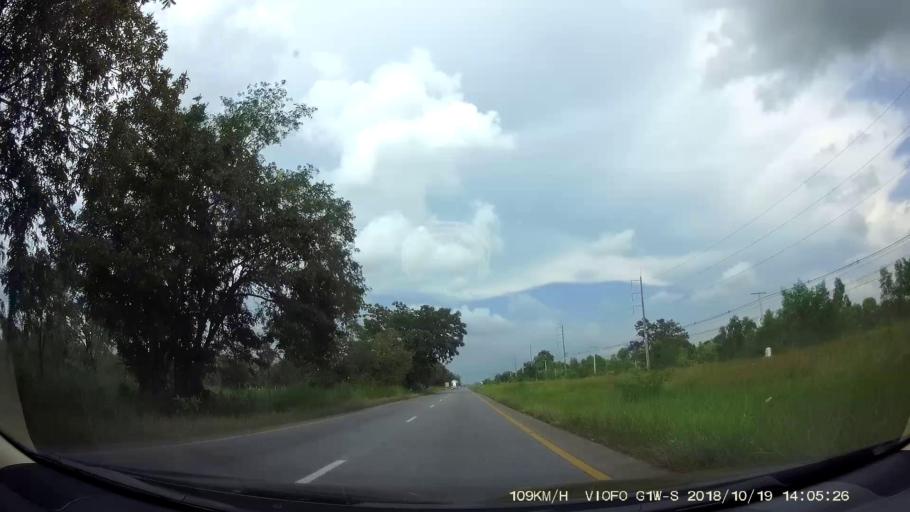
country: TH
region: Chaiyaphum
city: Chaiyaphum
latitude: 15.8752
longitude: 102.0930
